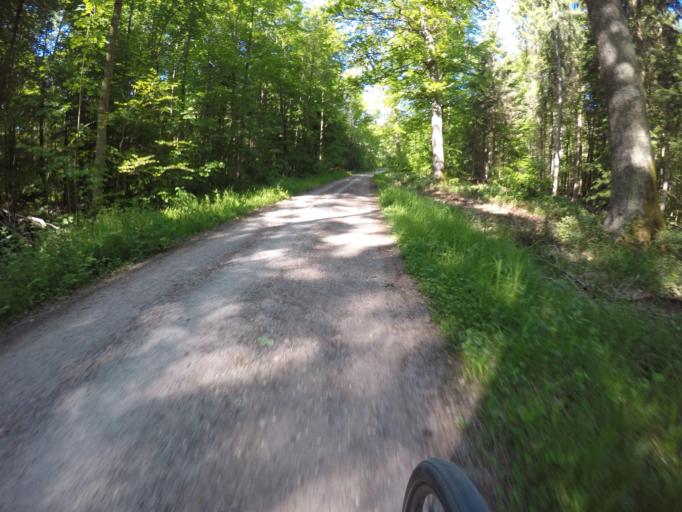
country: DE
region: Baden-Wuerttemberg
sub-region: Regierungsbezirk Stuttgart
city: Sindelfingen
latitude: 48.7432
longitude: 9.0520
